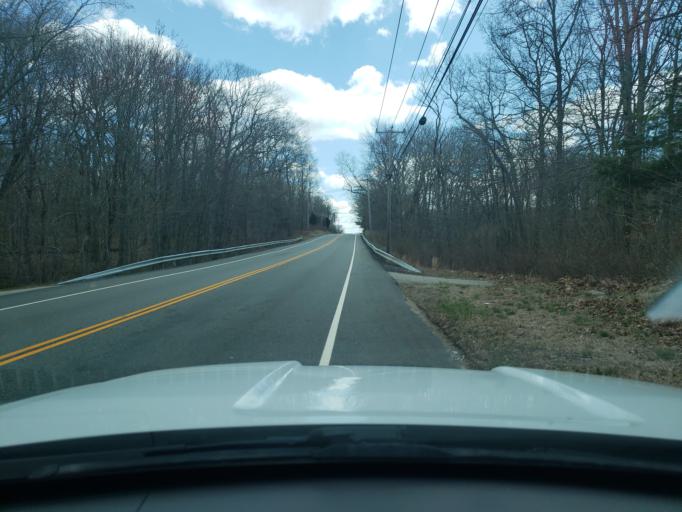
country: US
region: Connecticut
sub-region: New London County
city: Jewett City
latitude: 41.5791
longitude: -71.8915
